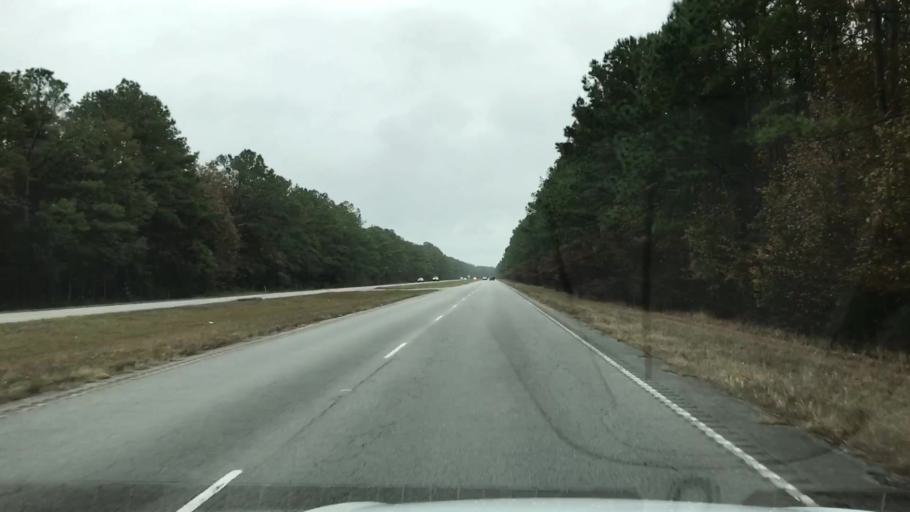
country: US
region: South Carolina
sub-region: Charleston County
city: Awendaw
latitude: 32.9628
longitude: -79.6846
